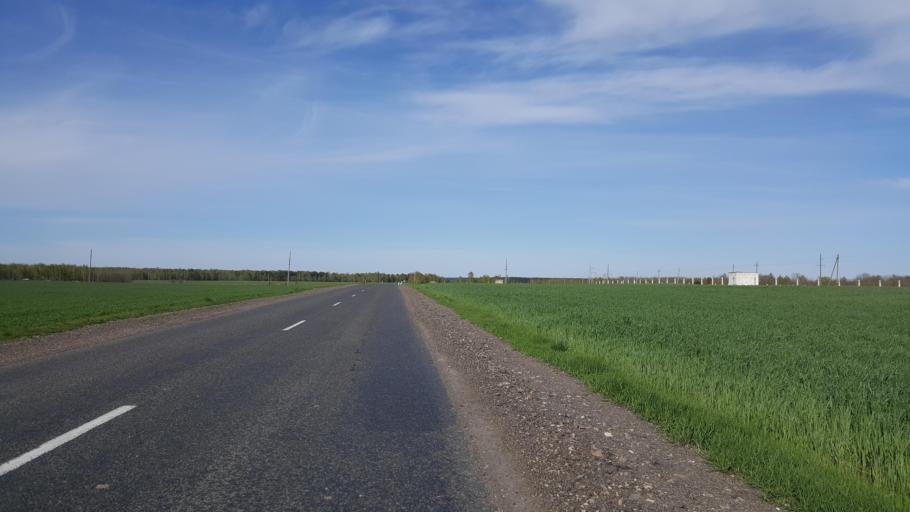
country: BY
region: Brest
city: Vysokaye
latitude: 52.3908
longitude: 23.4627
